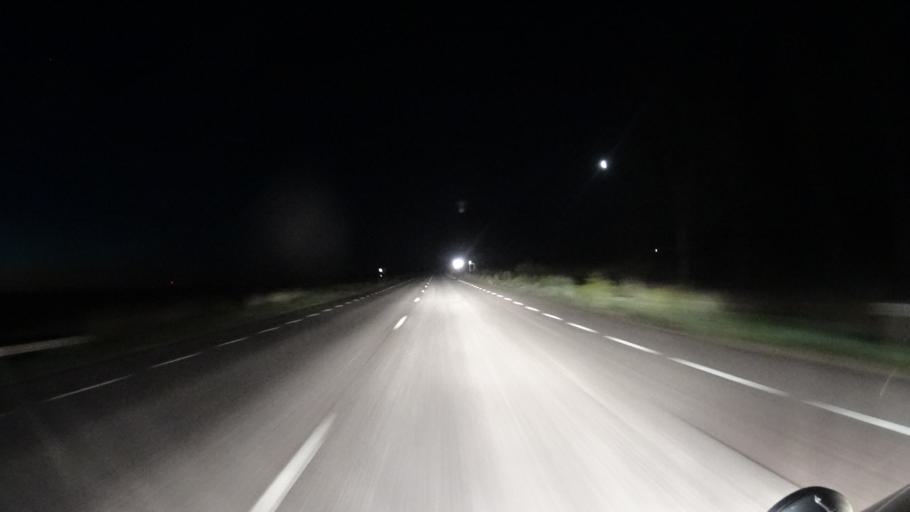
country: SE
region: OEstergoetland
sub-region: Vadstena Kommun
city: Herrestad
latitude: 58.3049
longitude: 14.8407
